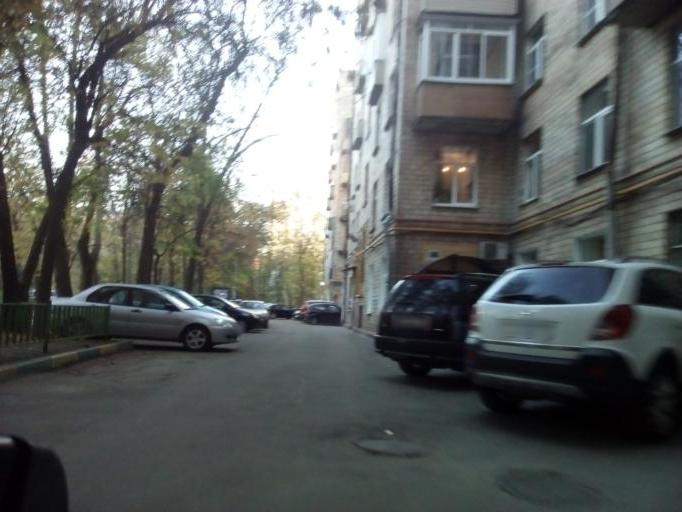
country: RU
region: Moskovskaya
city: Koptevo
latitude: 55.8231
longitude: 37.4925
